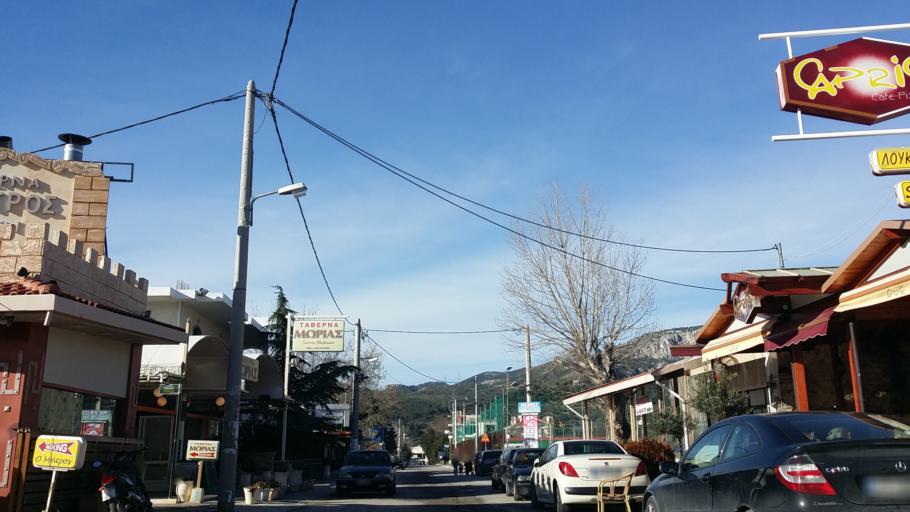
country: GR
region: Attica
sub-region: Nomarchia Dytikis Attikis
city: Fyli
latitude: 38.1060
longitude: 23.6683
